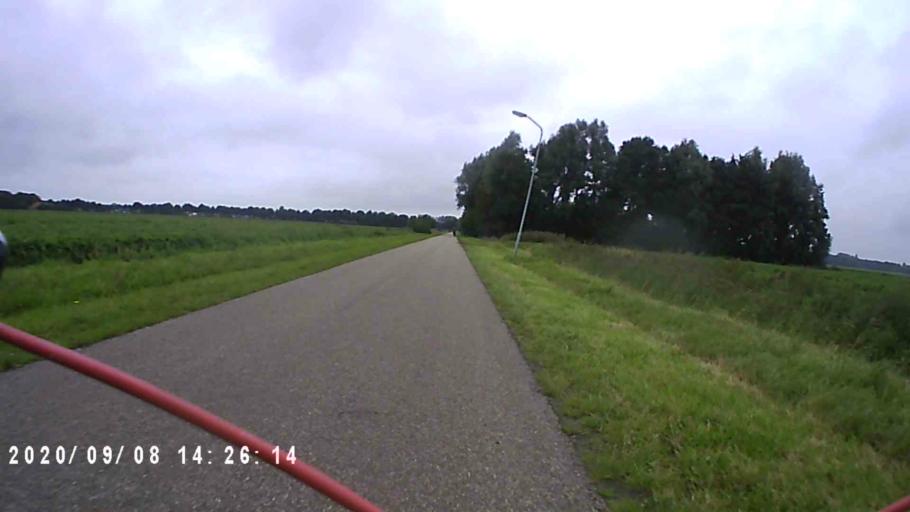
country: NL
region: Groningen
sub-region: Gemeente Slochteren
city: Slochteren
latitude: 53.2200
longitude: 6.8231
